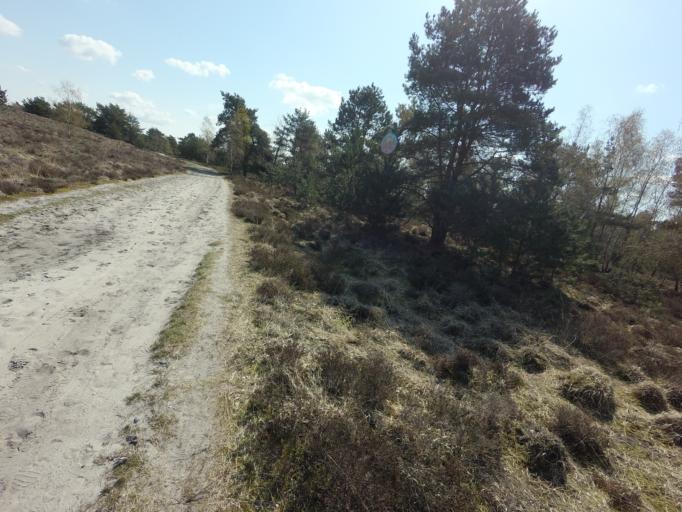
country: NL
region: Limburg
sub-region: Gemeente Bergen
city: Wellerlooi
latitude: 51.5943
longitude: 6.1023
